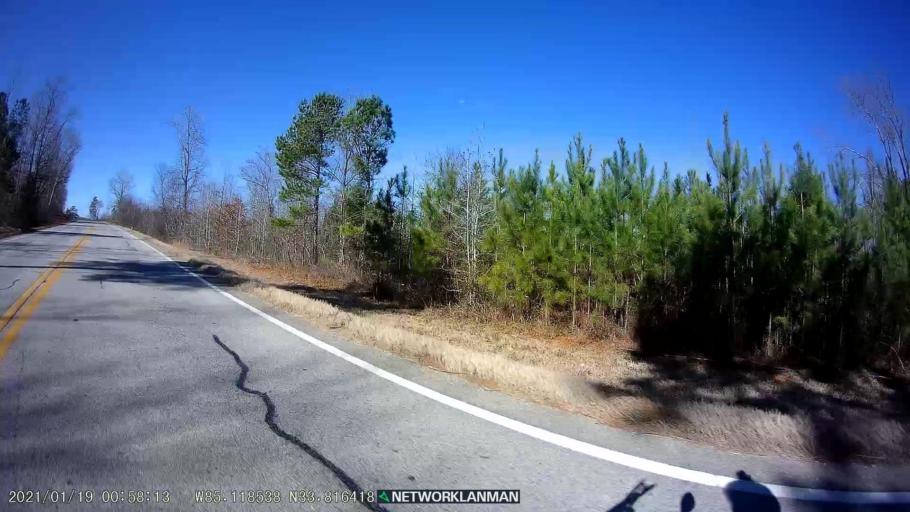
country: US
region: Georgia
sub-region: Haralson County
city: Buchanan
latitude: 33.8166
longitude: -85.1200
